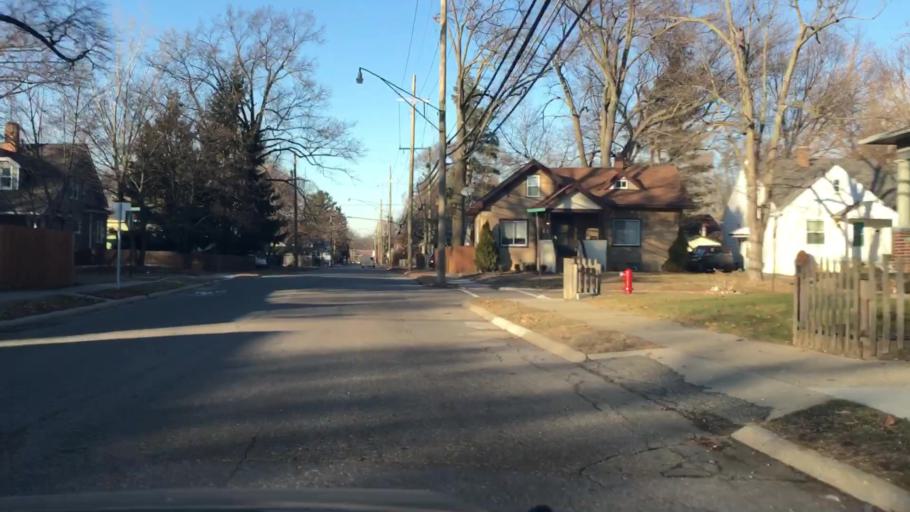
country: US
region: Michigan
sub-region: Oakland County
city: Ferndale
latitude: 42.4553
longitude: -83.1378
